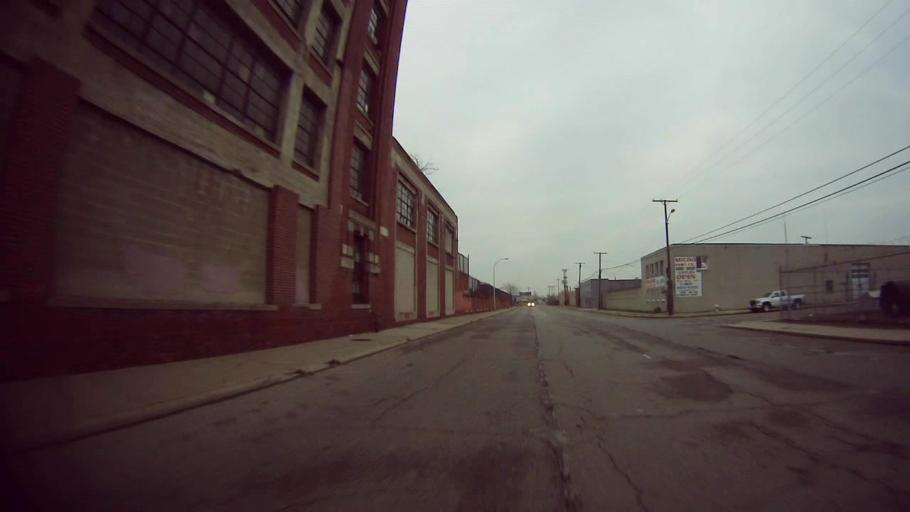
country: US
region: Michigan
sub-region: Wayne County
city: Highland Park
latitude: 42.4092
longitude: -83.0924
